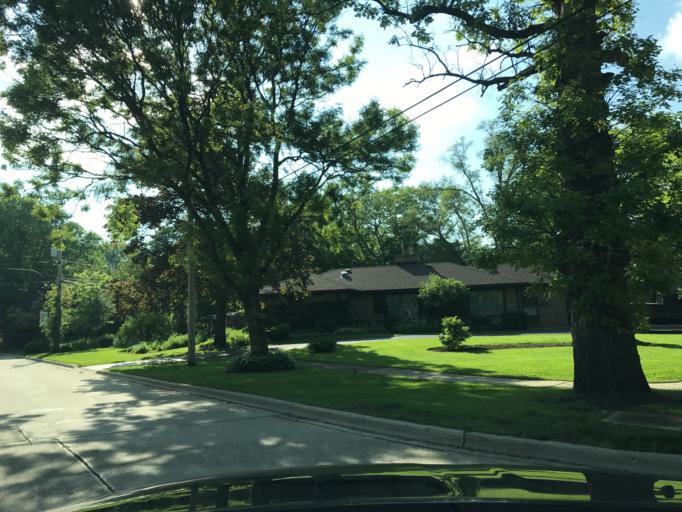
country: US
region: Illinois
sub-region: DuPage County
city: Naperville
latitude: 41.7698
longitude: -88.1359
